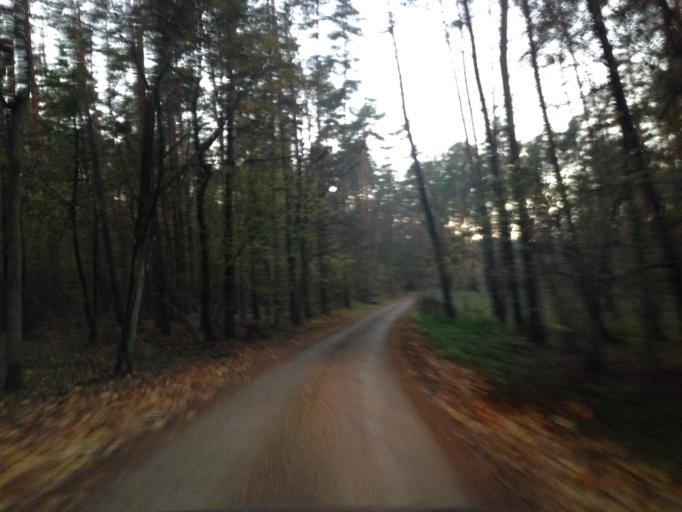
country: PL
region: Kujawsko-Pomorskie
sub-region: Powiat brodnicki
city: Gorzno
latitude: 53.2238
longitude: 19.6735
